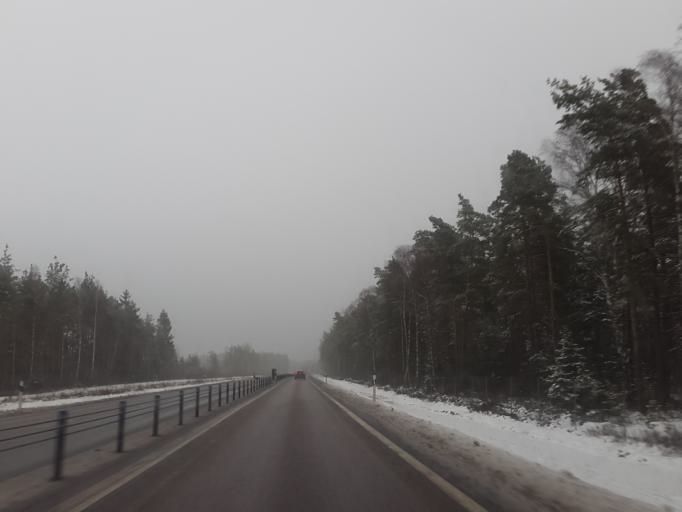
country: SE
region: Joenkoeping
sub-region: Jonkopings Kommun
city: Taberg
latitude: 57.7674
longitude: 14.0289
